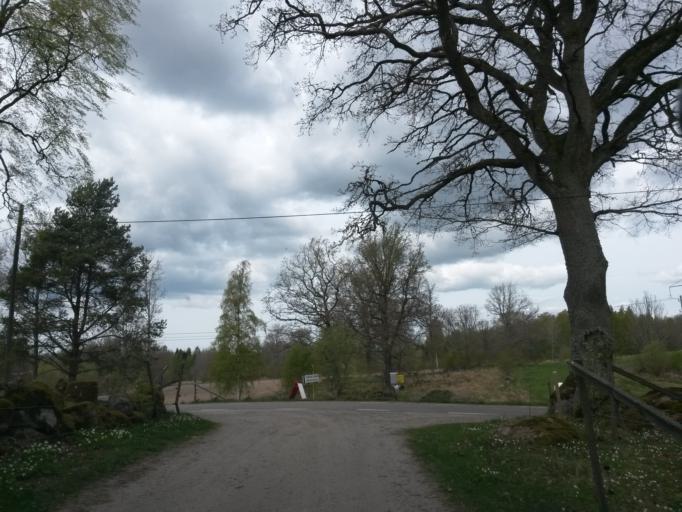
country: SE
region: Vaestra Goetaland
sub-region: Herrljunga Kommun
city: Herrljunga
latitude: 58.1421
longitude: 13.0501
